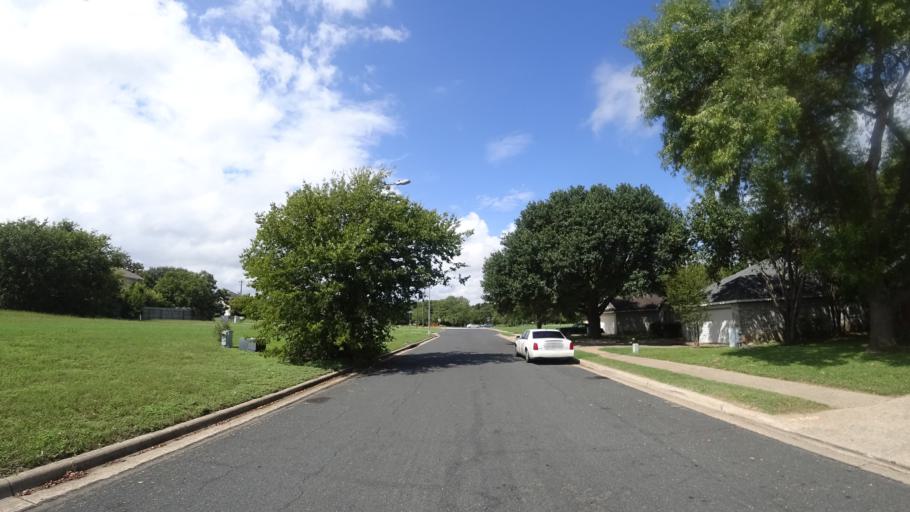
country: US
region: Texas
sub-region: Travis County
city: Onion Creek
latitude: 30.1664
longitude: -97.7395
